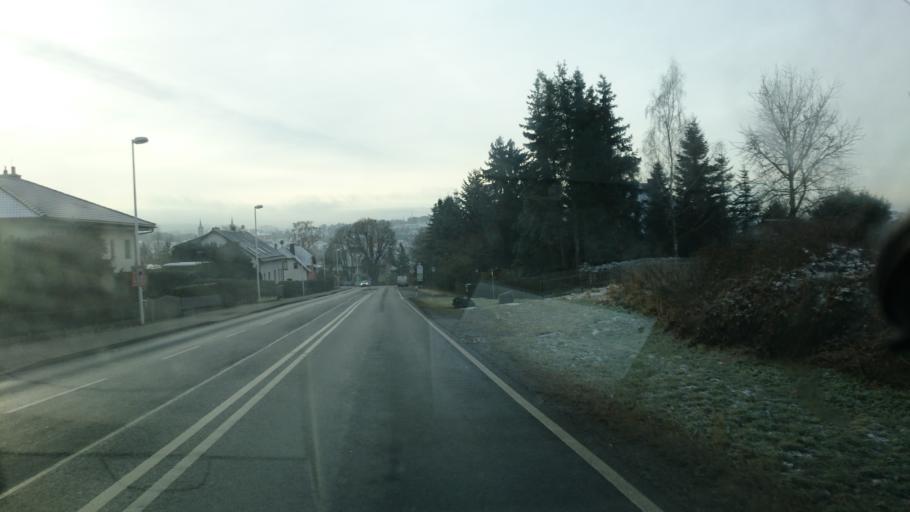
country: DE
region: Thuringia
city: Schleiz
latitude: 50.5867
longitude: 11.8114
